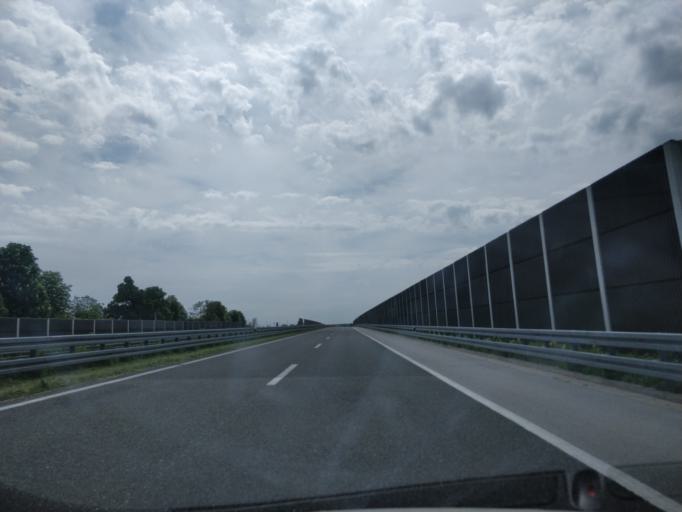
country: HR
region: Zagrebacka
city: Gradici
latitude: 45.7086
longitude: 16.0455
